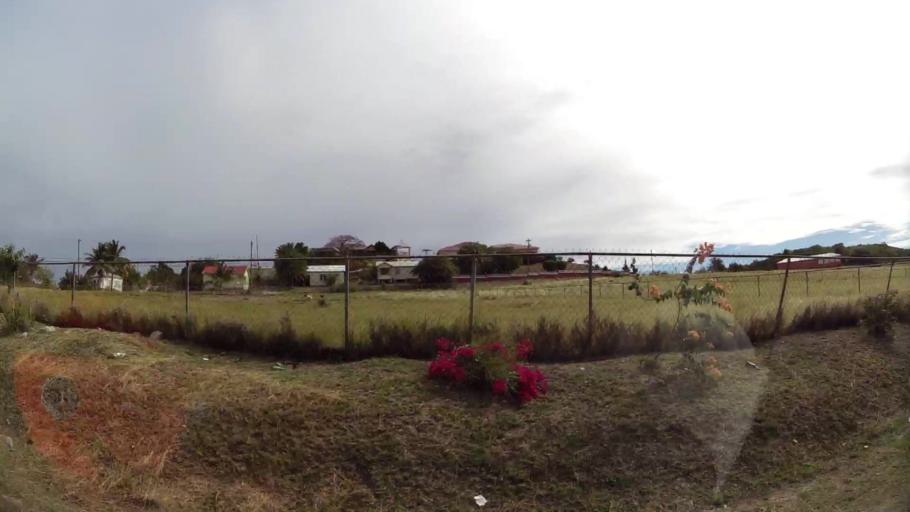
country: AG
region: Saint Peter
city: Parham
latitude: 17.0556
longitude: -61.7299
